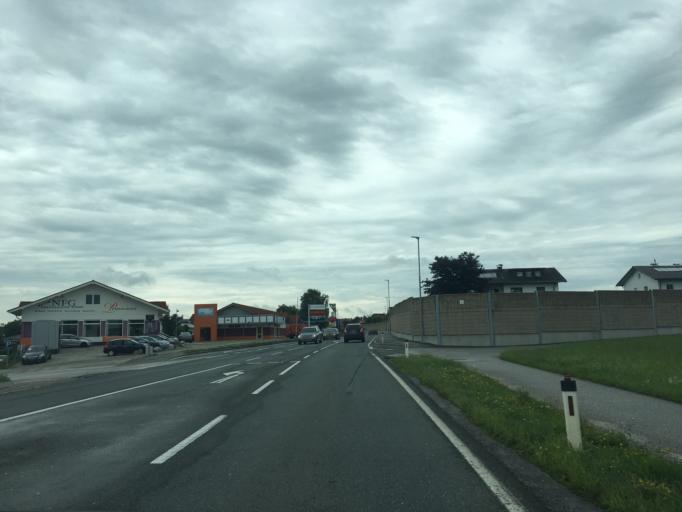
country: AT
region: Salzburg
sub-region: Politischer Bezirk Salzburg-Umgebung
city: Lamprechtshausen
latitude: 47.9843
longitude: 12.9541
